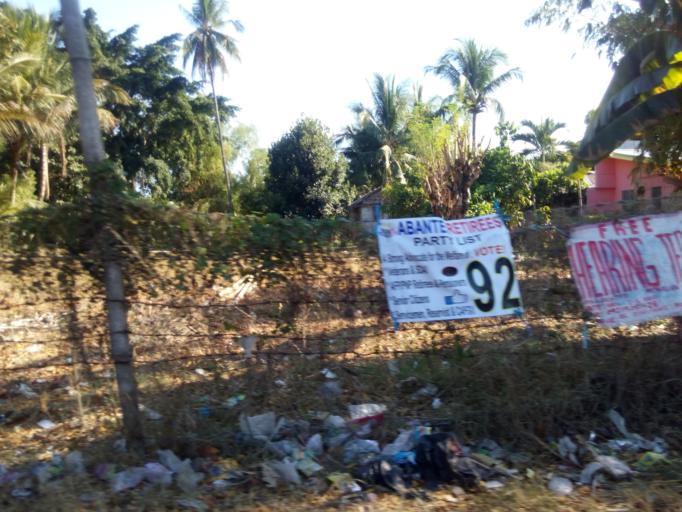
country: PH
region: Central Visayas
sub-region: Province of Negros Oriental
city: Valencia
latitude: 9.3130
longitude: 123.2637
